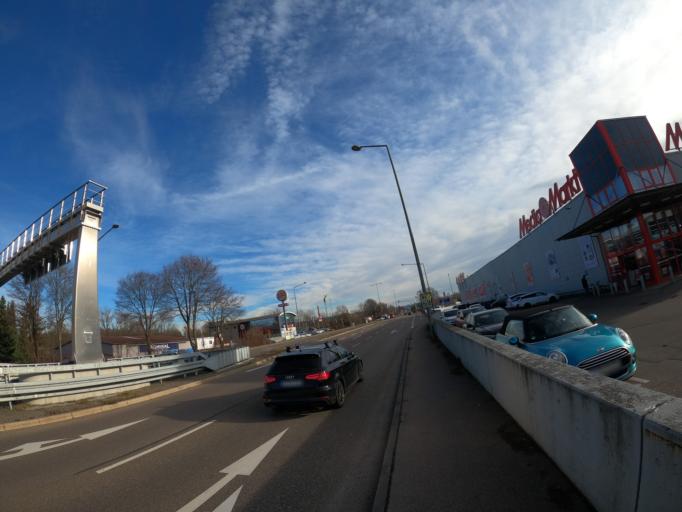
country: DE
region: Baden-Wuerttemberg
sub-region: Regierungsbezirk Stuttgart
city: Eislingen
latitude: 48.6972
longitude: 9.6870
